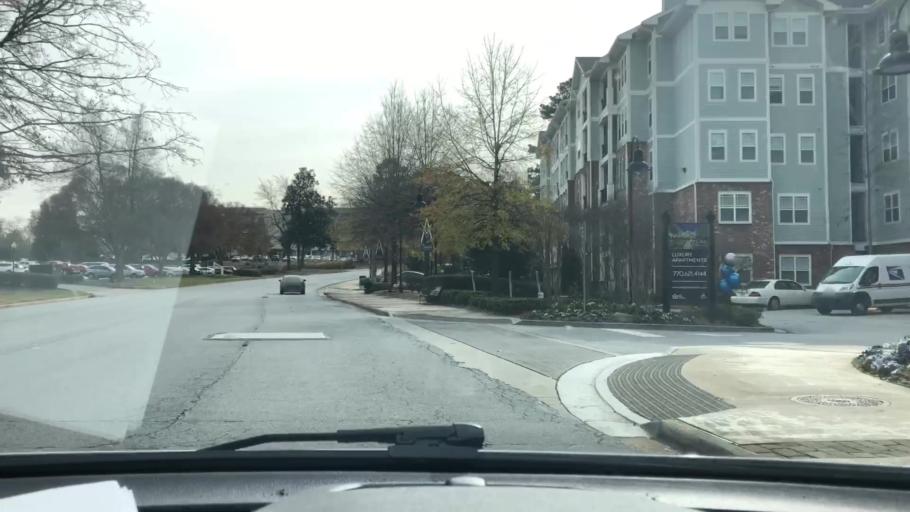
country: US
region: Georgia
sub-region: DeKalb County
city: Tucker
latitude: 33.8499
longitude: -84.2492
